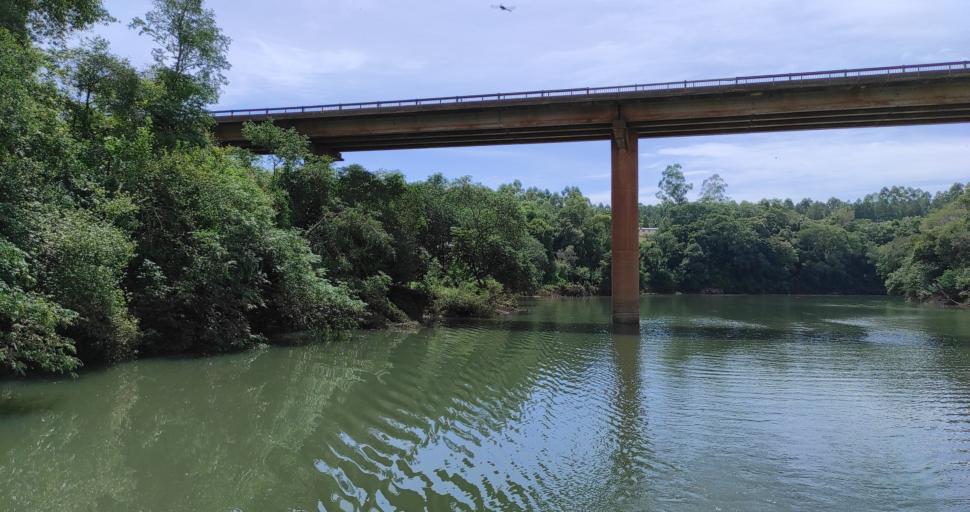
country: AR
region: Misiones
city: El Soberbio
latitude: -27.2803
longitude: -54.1973
